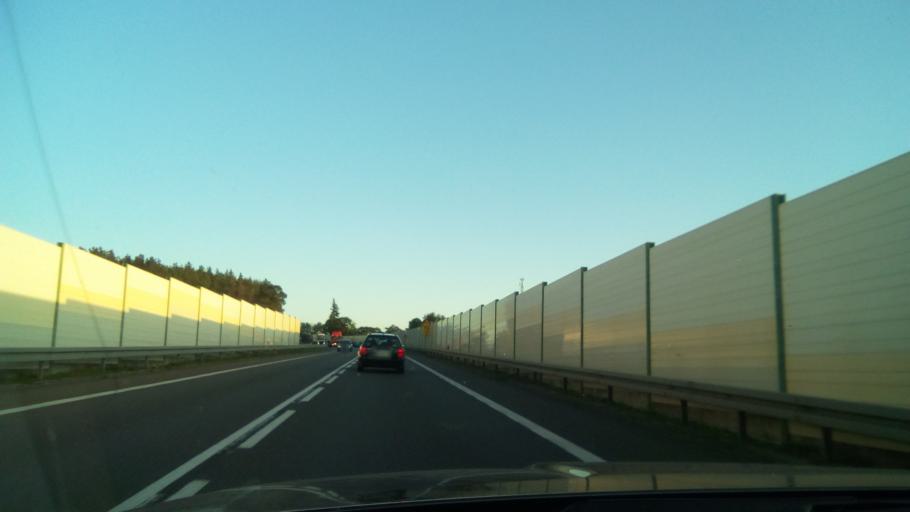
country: PL
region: West Pomeranian Voivodeship
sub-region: Powiat kamienski
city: Wolin
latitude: 53.8714
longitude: 14.5401
